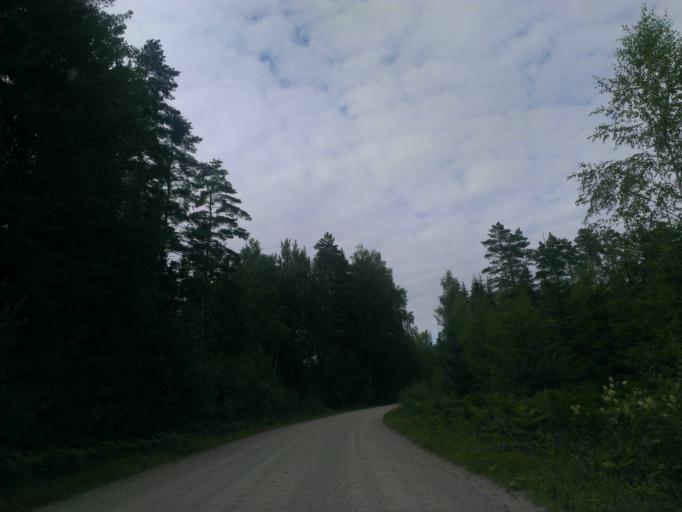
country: LV
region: Incukalns
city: Vangazi
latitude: 57.0952
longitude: 24.5627
